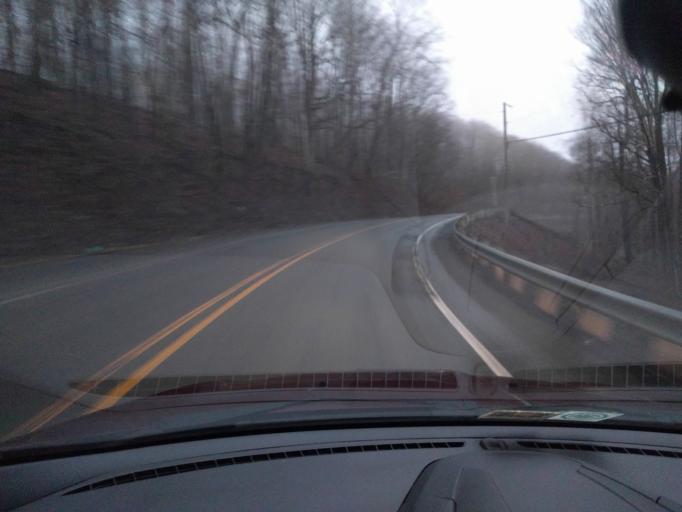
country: US
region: West Virginia
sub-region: Greenbrier County
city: Rainelle
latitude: 37.9853
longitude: -80.8484
